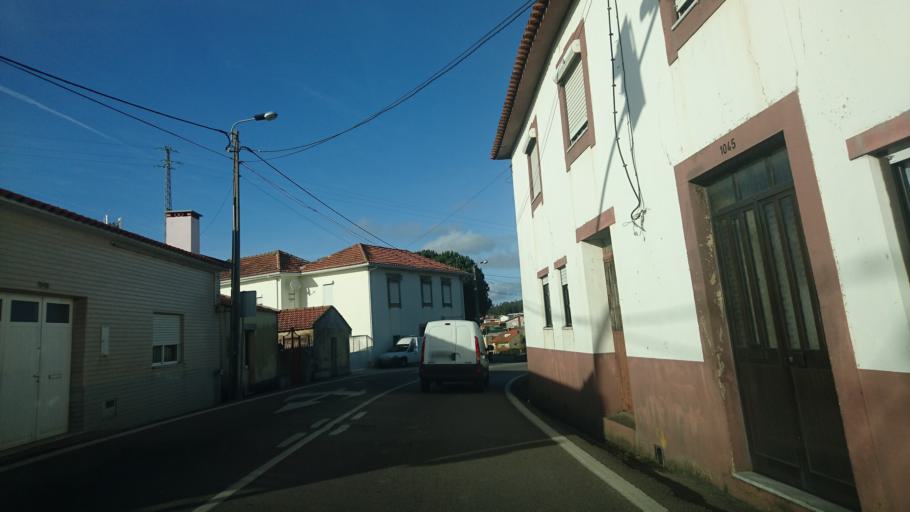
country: PT
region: Aveiro
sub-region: Espinho
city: Souto
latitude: 40.9752
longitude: -8.6305
